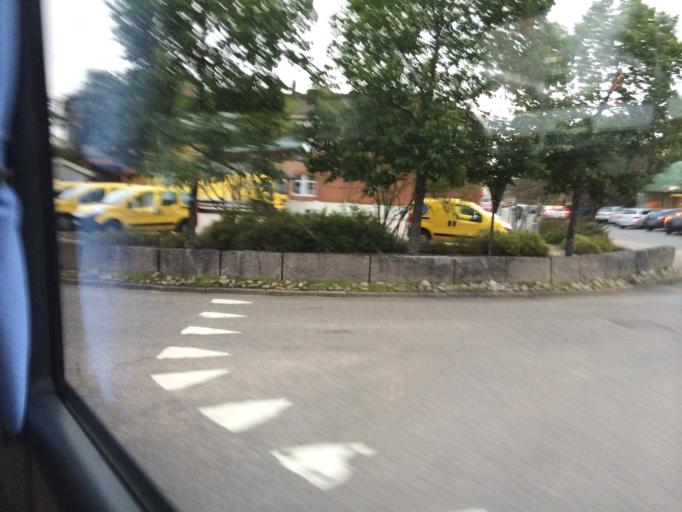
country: SE
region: Vaestra Goetaland
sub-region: Tranemo Kommun
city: Tranemo
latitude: 57.4833
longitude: 13.3507
